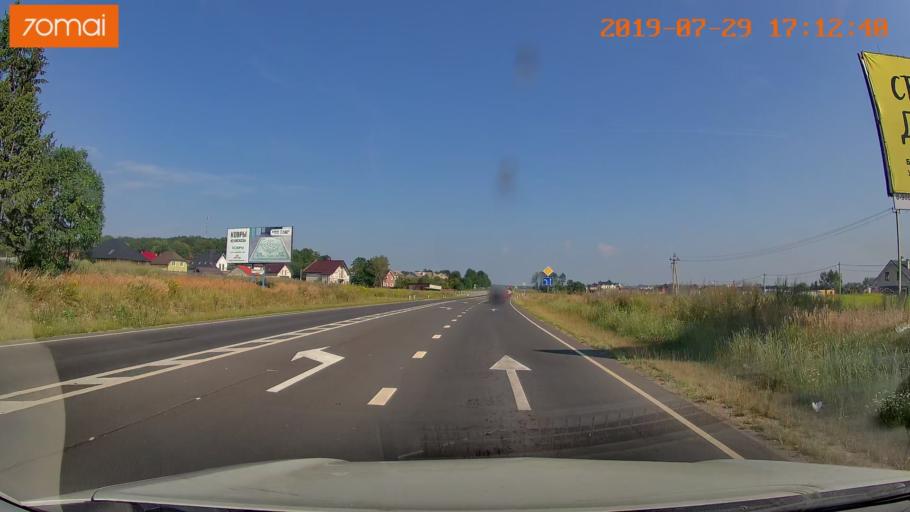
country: RU
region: Kaliningrad
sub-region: Gorod Kaliningrad
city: Kaliningrad
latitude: 54.7870
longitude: 20.4012
